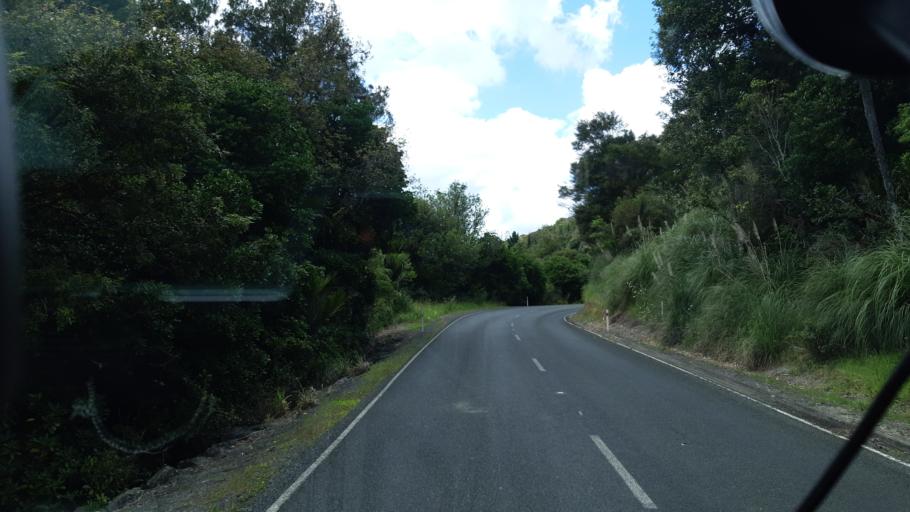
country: NZ
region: Northland
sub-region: Far North District
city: Taipa
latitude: -35.2501
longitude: 173.5315
